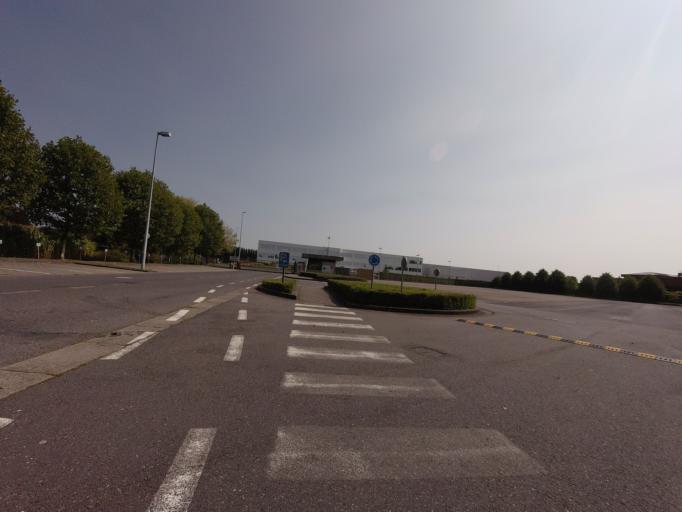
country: BE
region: Flanders
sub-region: Provincie Antwerpen
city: Aartselaar
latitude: 51.1502
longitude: 4.3960
